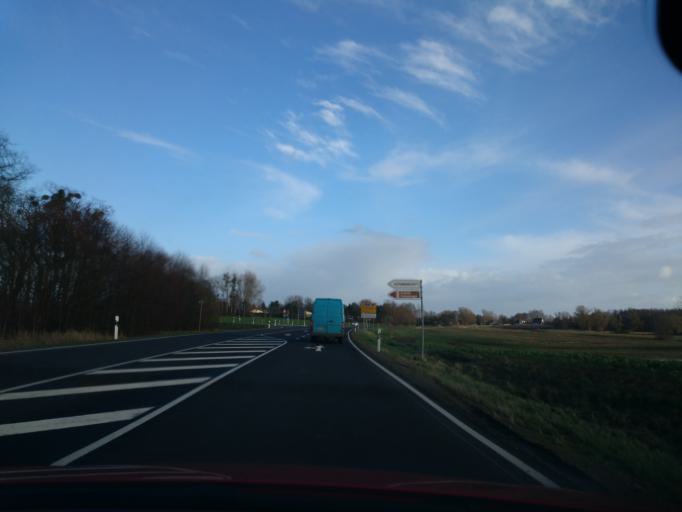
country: DE
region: Mecklenburg-Vorpommern
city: Brandshagen
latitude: 54.2166
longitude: 13.2415
